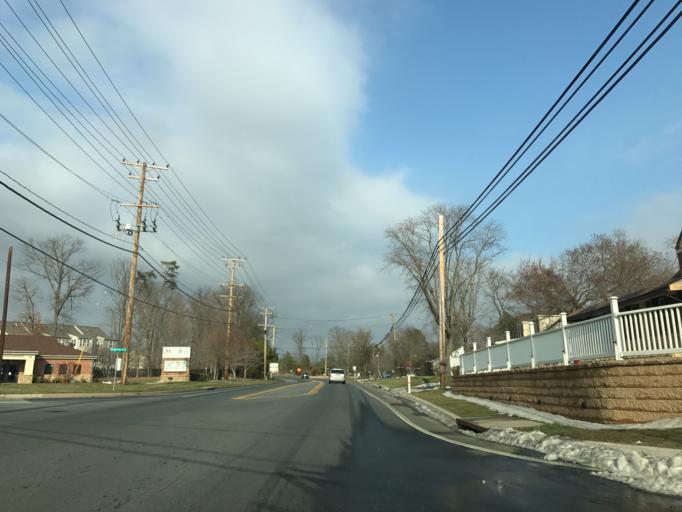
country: US
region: Maryland
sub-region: Harford County
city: Perryman
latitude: 39.4894
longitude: -76.2118
